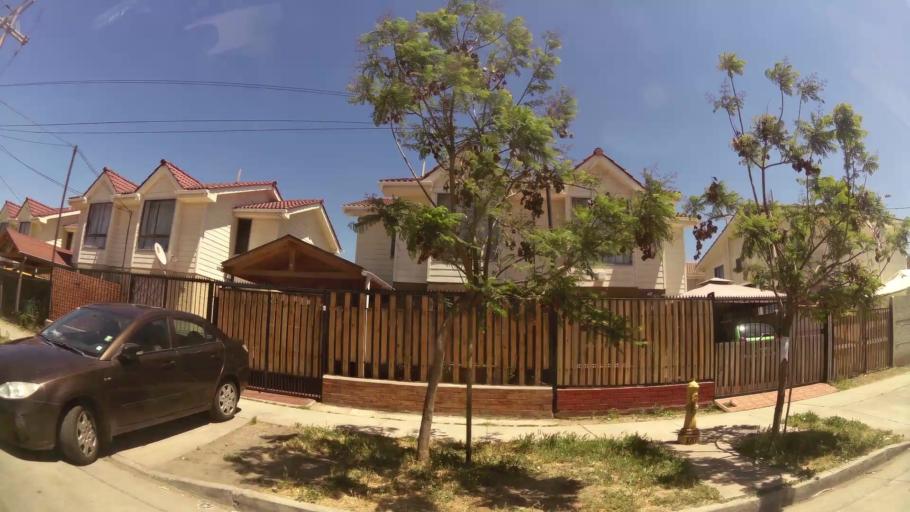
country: CL
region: Santiago Metropolitan
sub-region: Provincia de Maipo
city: San Bernardo
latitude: -33.6175
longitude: -70.7078
